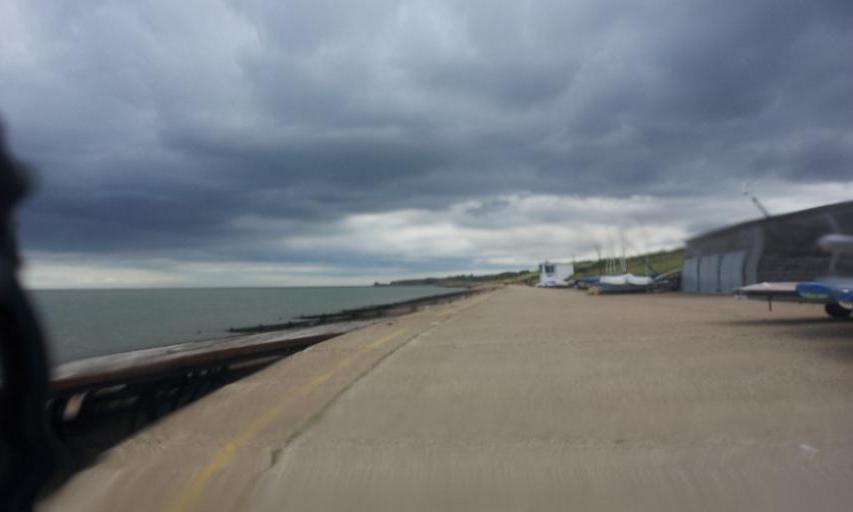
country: GB
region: England
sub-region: Kent
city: Herne Bay
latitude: 51.3729
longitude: 1.1395
